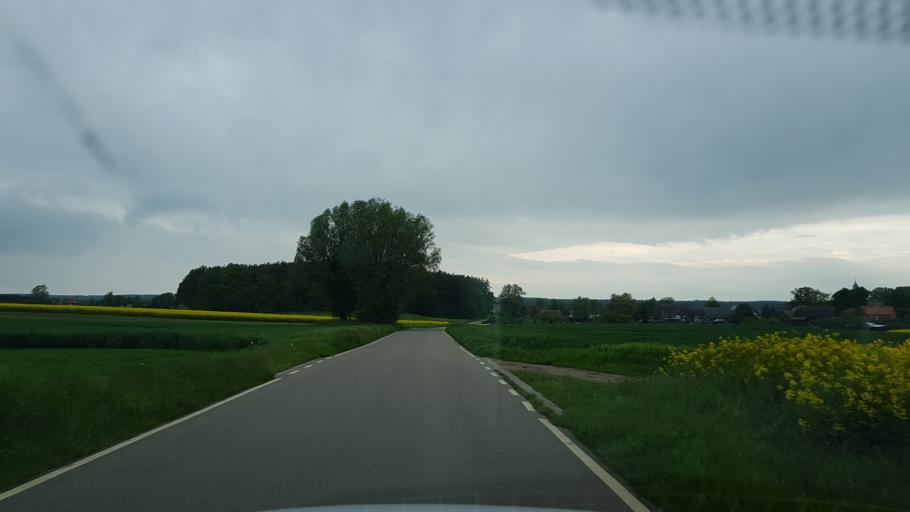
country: PL
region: West Pomeranian Voivodeship
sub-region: Powiat pyrzycki
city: Bielice
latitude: 53.1292
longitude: 14.7499
